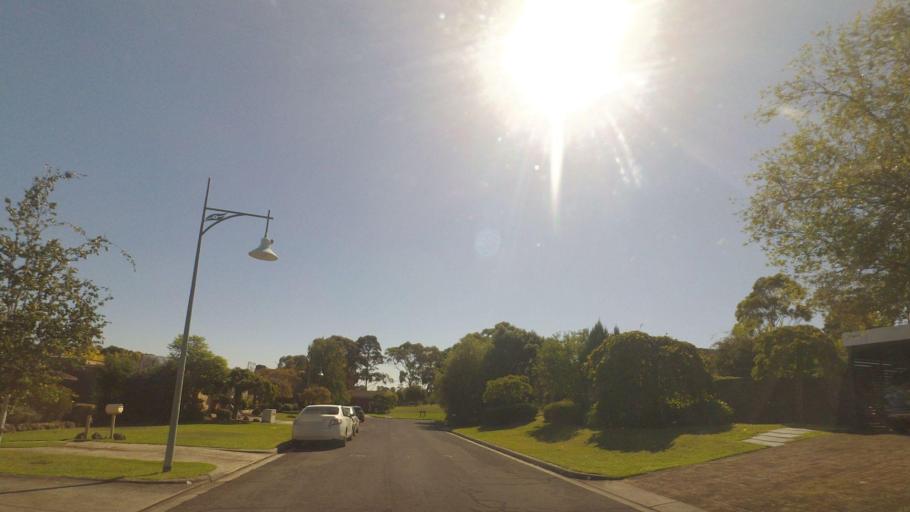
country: AU
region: Victoria
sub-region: Manningham
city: Donvale
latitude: -37.7778
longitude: 145.1716
